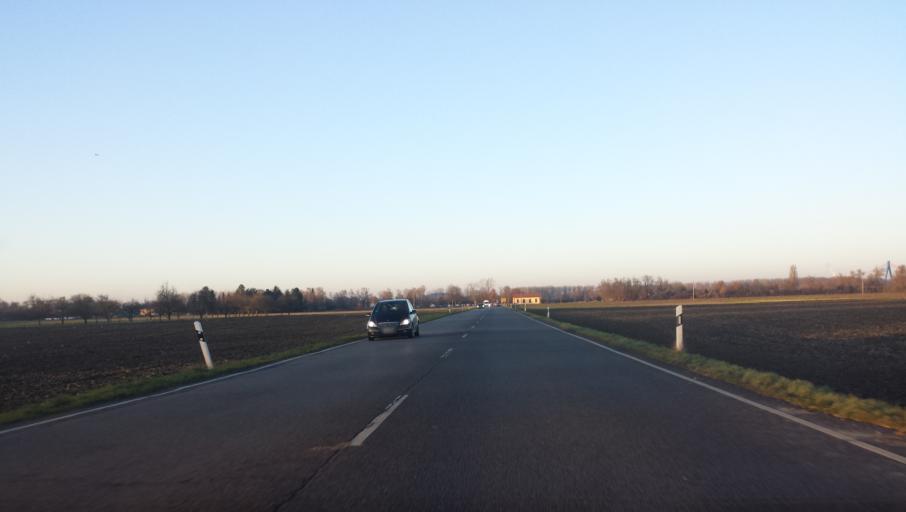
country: DE
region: Baden-Wuerttemberg
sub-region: Karlsruhe Region
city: Altlussheim
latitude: 49.3156
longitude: 8.4684
